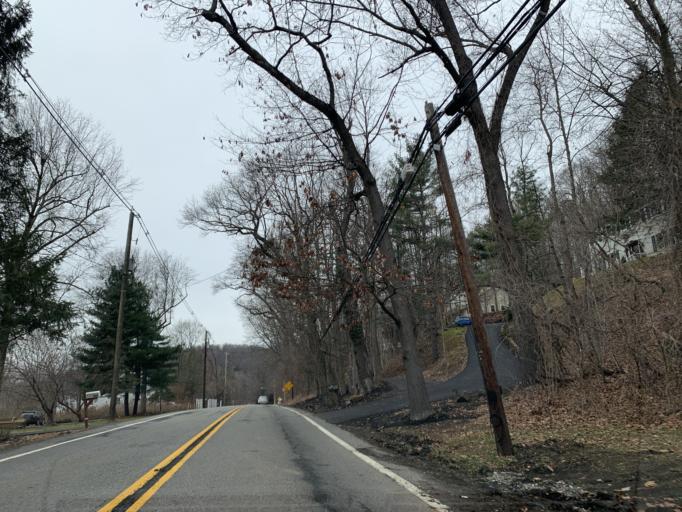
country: US
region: New Jersey
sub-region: Somerset County
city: Green Knoll
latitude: 40.6393
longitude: -74.6131
